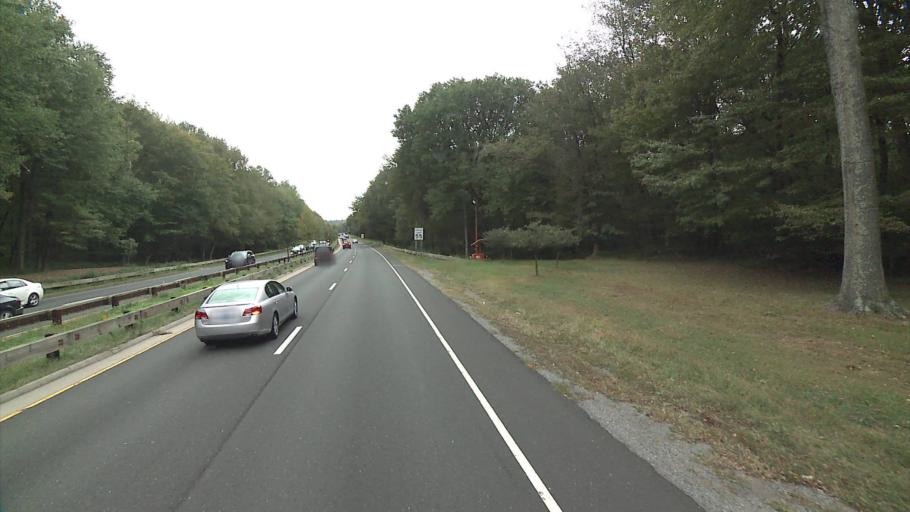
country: US
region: Connecticut
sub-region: Fairfield County
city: Southport
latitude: 41.1931
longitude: -73.2909
